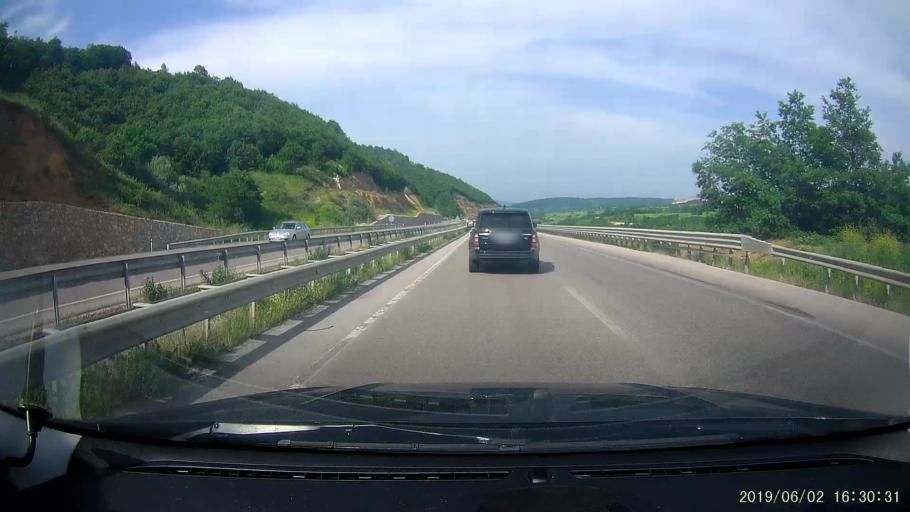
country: TR
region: Samsun
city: Ladik
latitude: 41.0258
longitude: 35.8840
